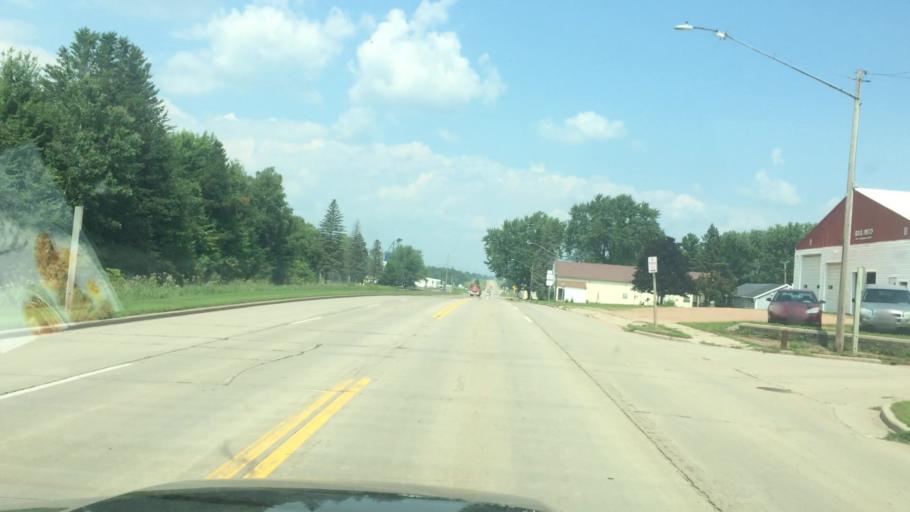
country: US
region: Wisconsin
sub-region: Clark County
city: Colby
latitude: 44.8484
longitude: -90.3160
